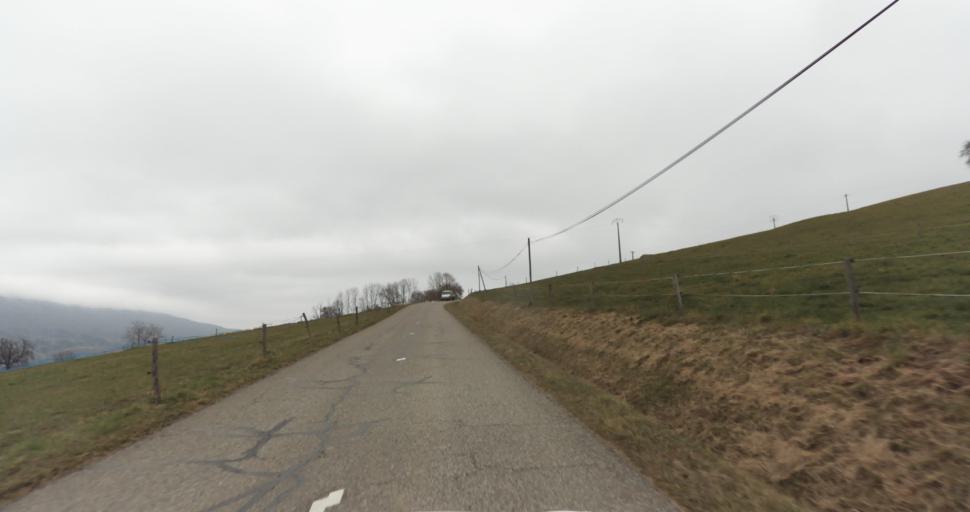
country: FR
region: Rhone-Alpes
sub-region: Departement de la Haute-Savoie
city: Saint-Jorioz
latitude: 45.8012
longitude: 6.1576
